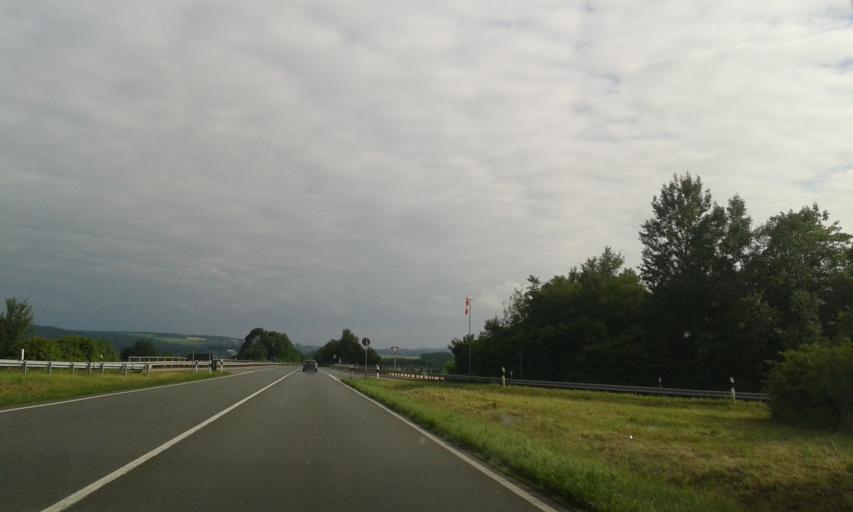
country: DE
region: Lower Saxony
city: Rinteln
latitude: 52.1961
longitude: 9.0948
